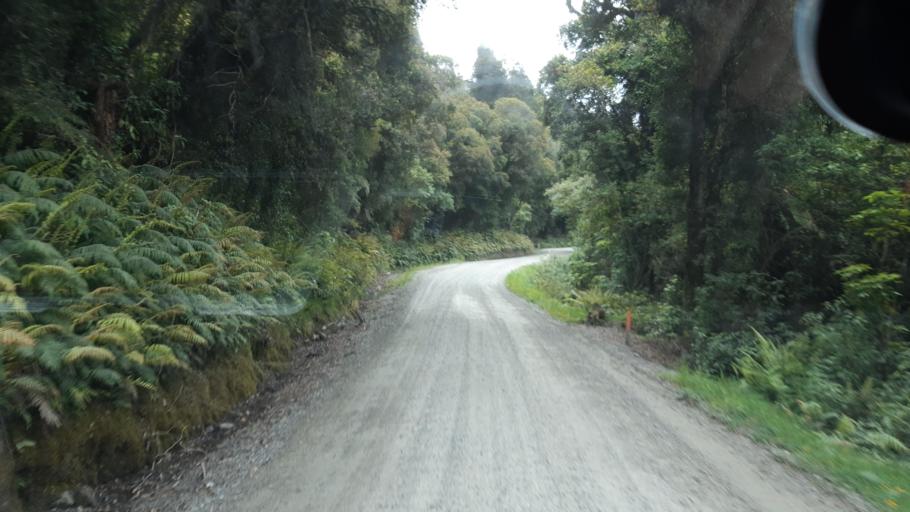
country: NZ
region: West Coast
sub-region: Grey District
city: Greymouth
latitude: -42.6375
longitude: 171.3862
